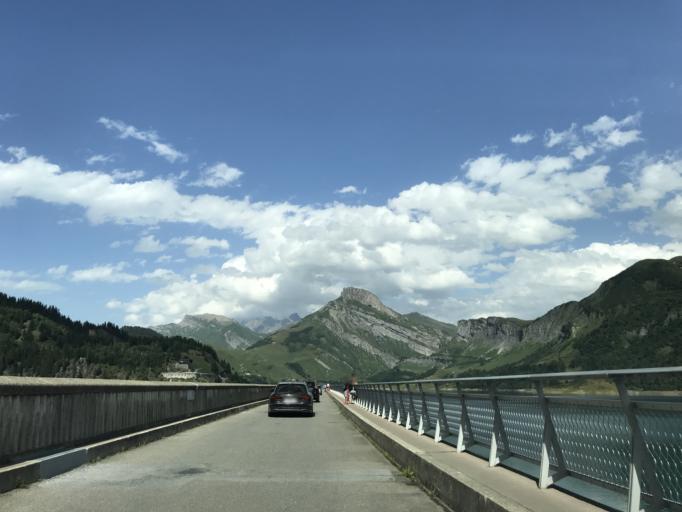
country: FR
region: Rhone-Alpes
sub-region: Departement de la Savoie
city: Beaufort
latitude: 45.6831
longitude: 6.6178
